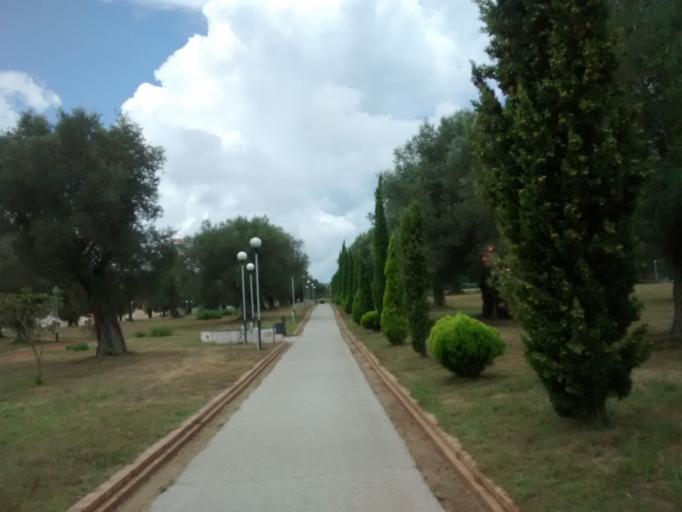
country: IT
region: Calabria
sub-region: Provincia di Vibo-Valentia
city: Vibo Valentia
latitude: 38.6633
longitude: 16.0788
